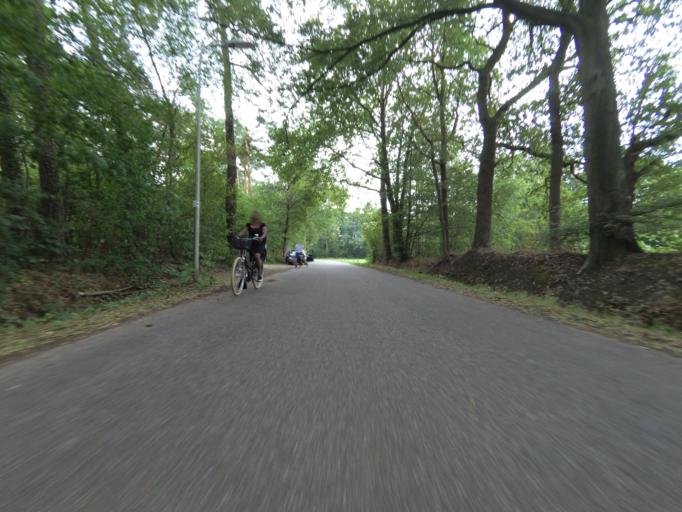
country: NL
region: Overijssel
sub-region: Gemeente Hengelo
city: Hengelo
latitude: 52.2584
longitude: 6.8402
